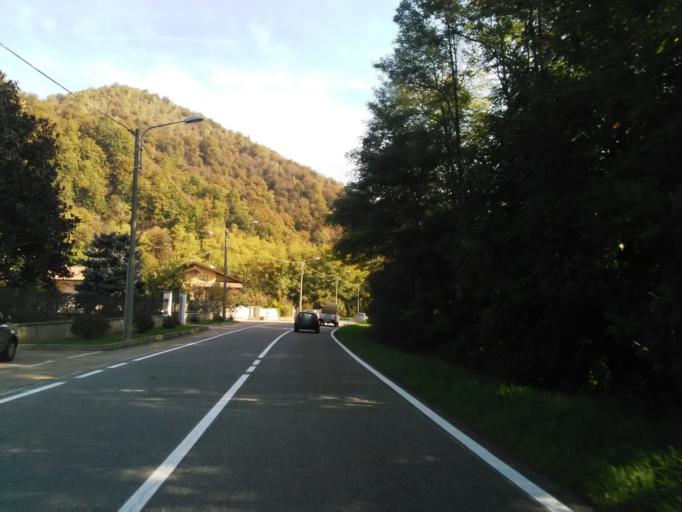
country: IT
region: Piedmont
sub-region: Provincia di Vercelli
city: Guardabosone
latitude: 45.6983
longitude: 8.2703
